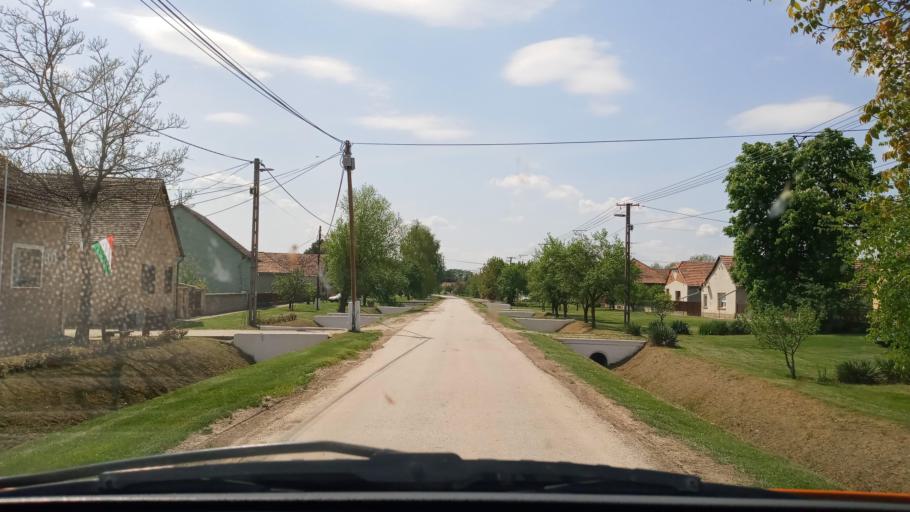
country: HU
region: Baranya
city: Villany
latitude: 45.8196
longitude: 18.4996
